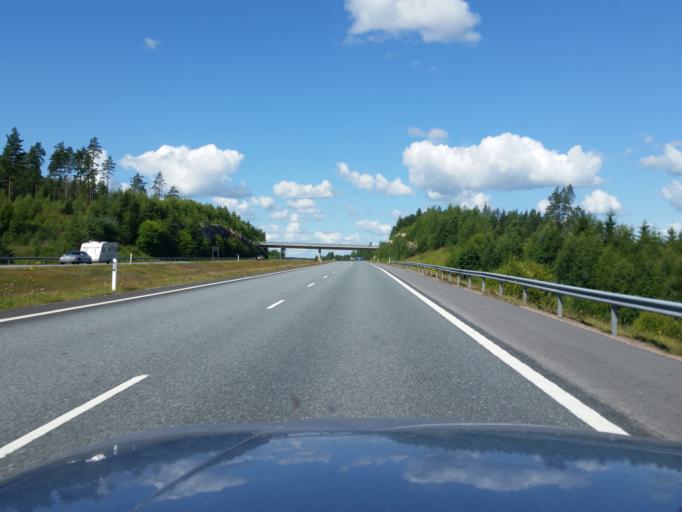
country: FI
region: Varsinais-Suomi
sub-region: Salo
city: Pertteli
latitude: 60.4030
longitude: 23.2269
